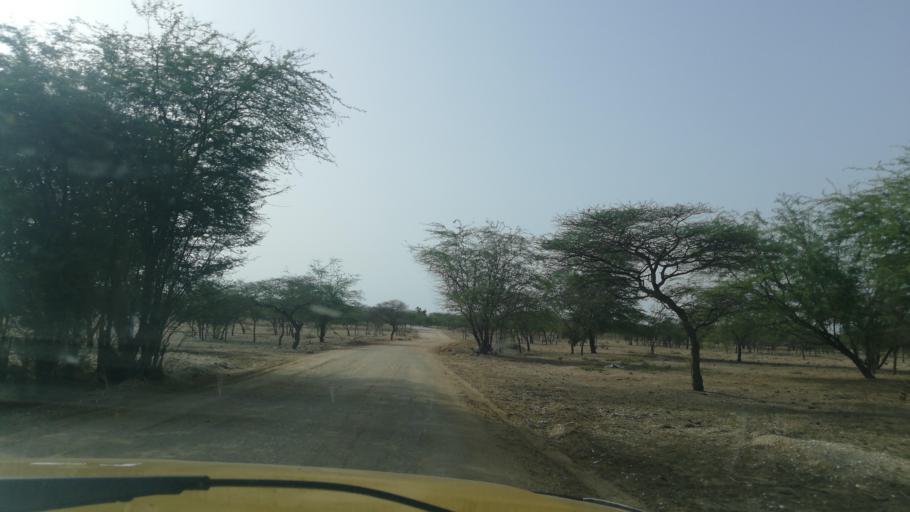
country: SN
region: Saint-Louis
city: Saint-Louis
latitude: 16.0618
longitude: -16.3344
